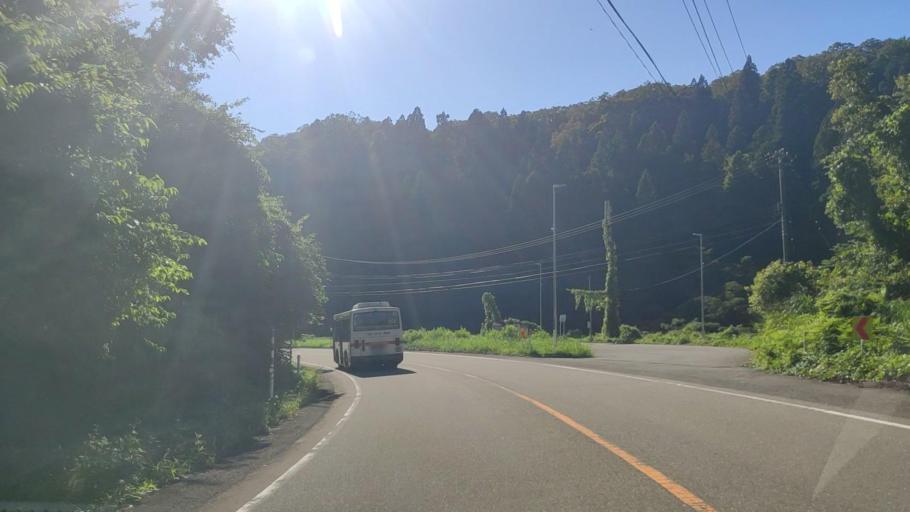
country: JP
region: Ishikawa
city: Nanao
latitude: 37.2417
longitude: 136.9806
